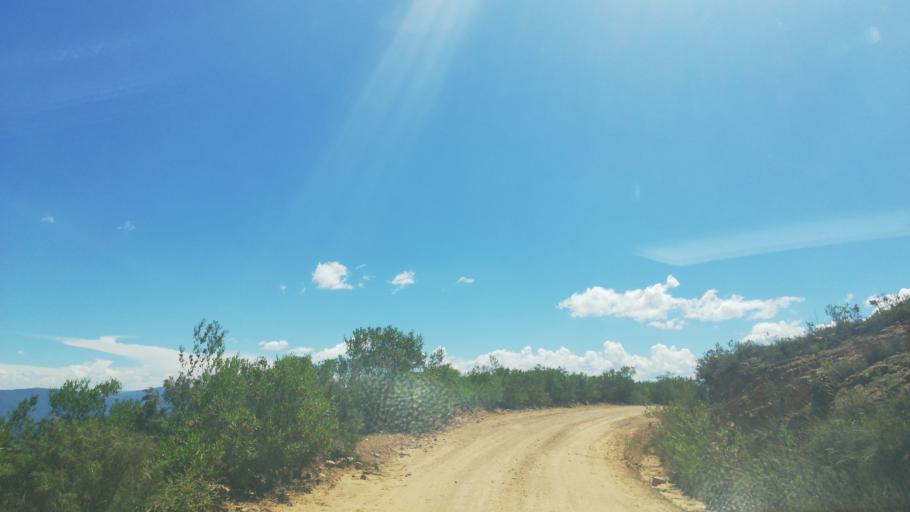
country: BO
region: Cochabamba
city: Totora
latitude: -17.7357
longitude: -65.2243
